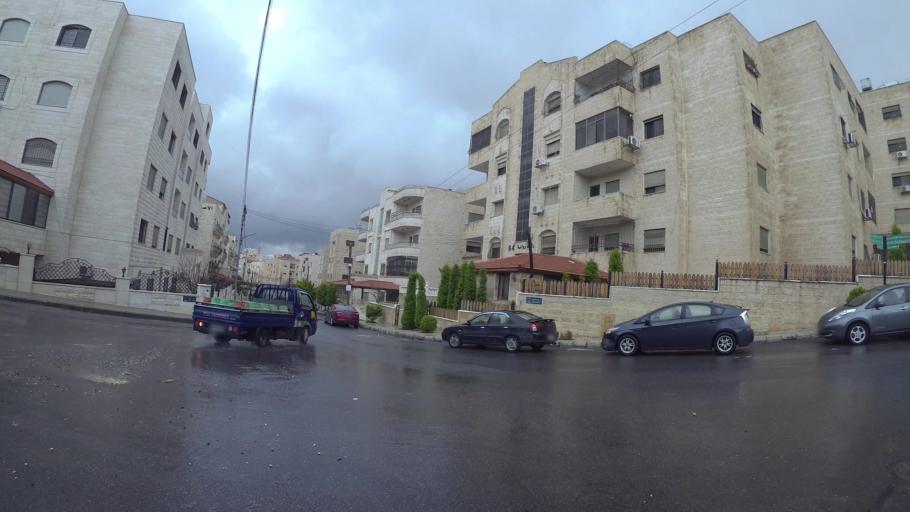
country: JO
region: Amman
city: Al Jubayhah
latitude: 32.0326
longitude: 35.8672
